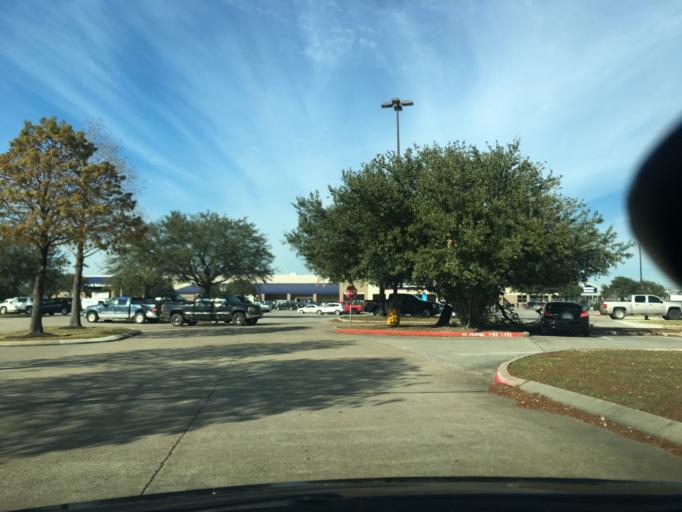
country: US
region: Texas
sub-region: Harris County
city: Cloverleaf
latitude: 29.8110
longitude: -95.1651
